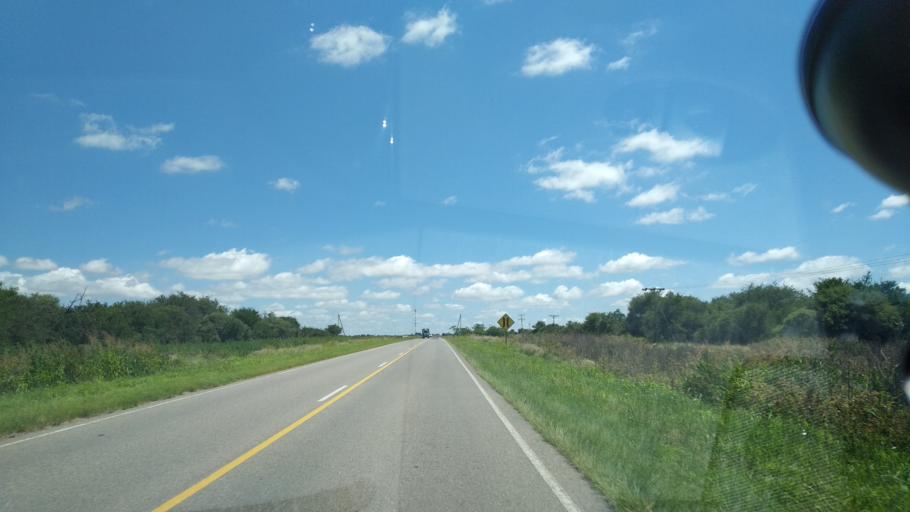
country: AR
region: Cordoba
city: Salsacate
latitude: -31.4866
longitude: -65.1080
